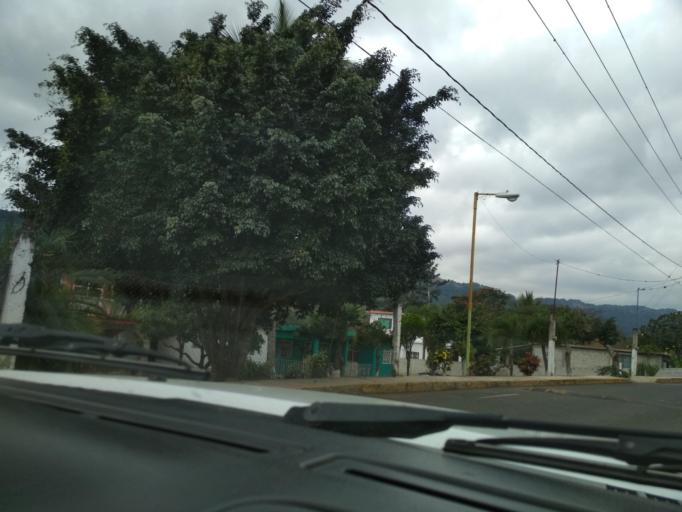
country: MX
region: Veracruz
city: El Castillo
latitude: 19.5831
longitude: -96.8402
